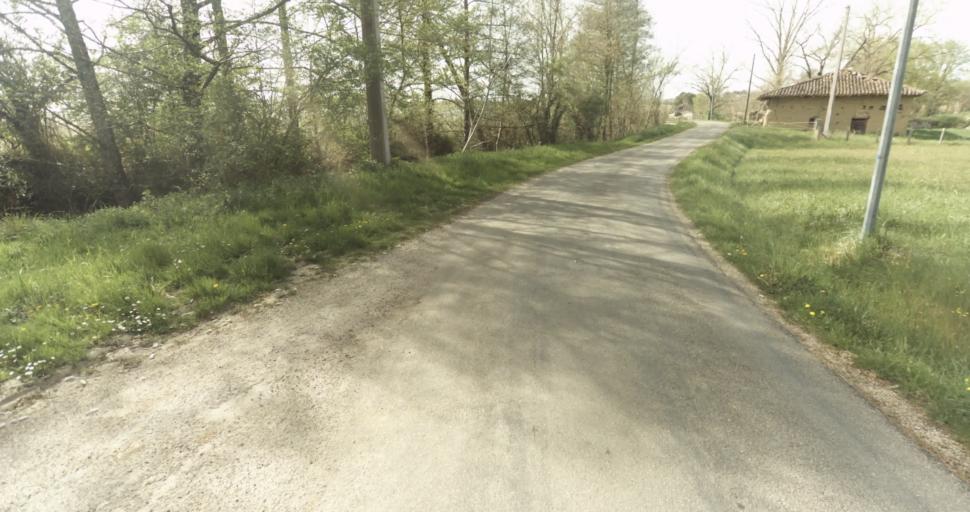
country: FR
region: Midi-Pyrenees
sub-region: Departement du Tarn-et-Garonne
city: Lafrancaise
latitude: 44.1371
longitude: 1.1771
